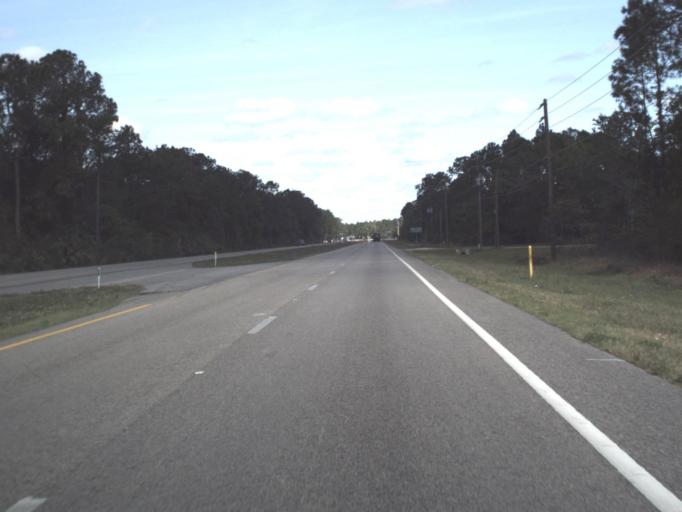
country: US
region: Florida
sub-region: Flagler County
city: Bunnell
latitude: 29.4128
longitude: -81.2050
